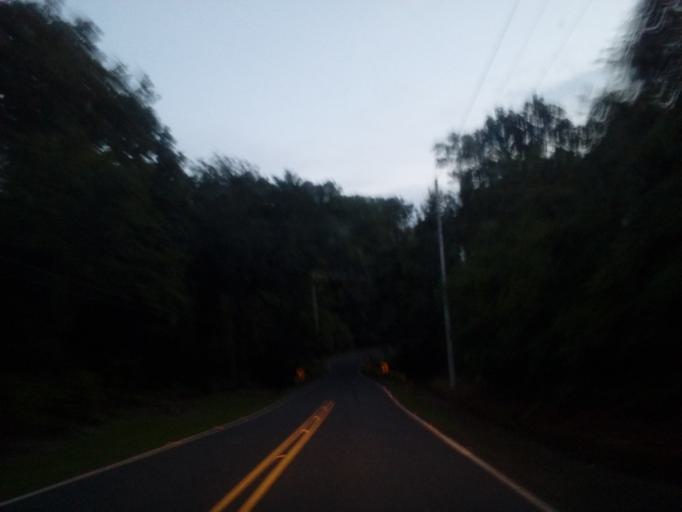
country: CR
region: Guanacaste
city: Samara
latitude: 9.9507
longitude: -85.5179
